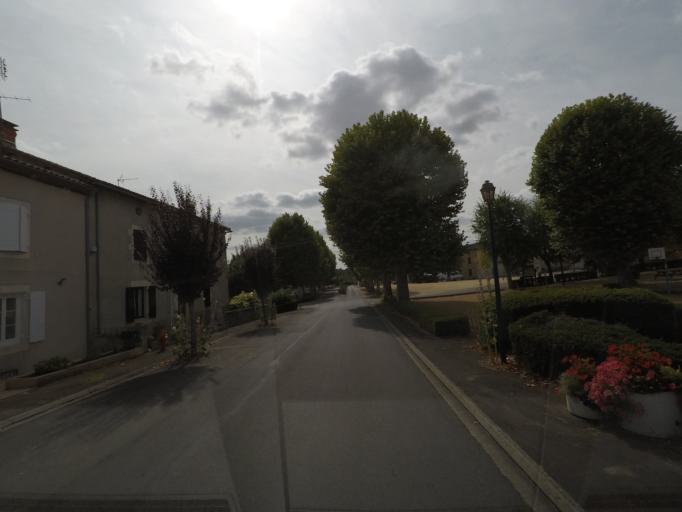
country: FR
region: Poitou-Charentes
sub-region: Departement de la Charente
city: Saint-Claud
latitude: 45.9415
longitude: 0.4841
